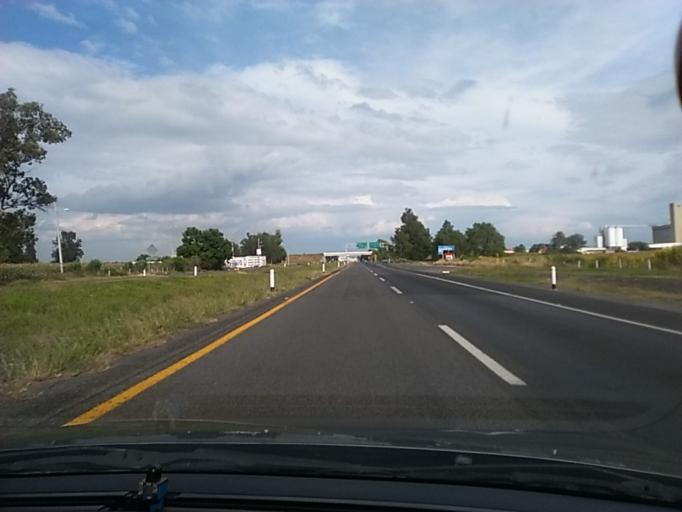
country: MX
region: Jalisco
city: La Barca
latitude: 20.3220
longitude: -102.5408
